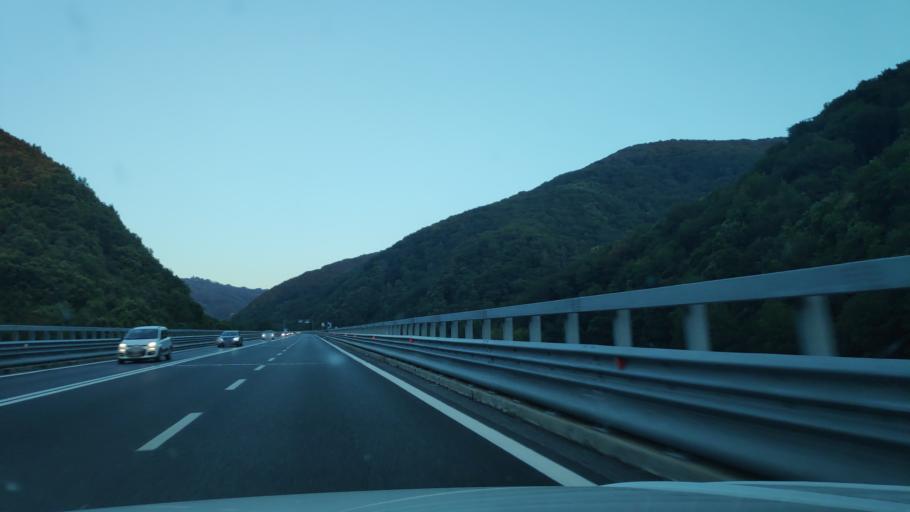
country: IT
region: Calabria
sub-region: Provincia di Reggio Calabria
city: Amato
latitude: 38.4078
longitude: 16.1476
